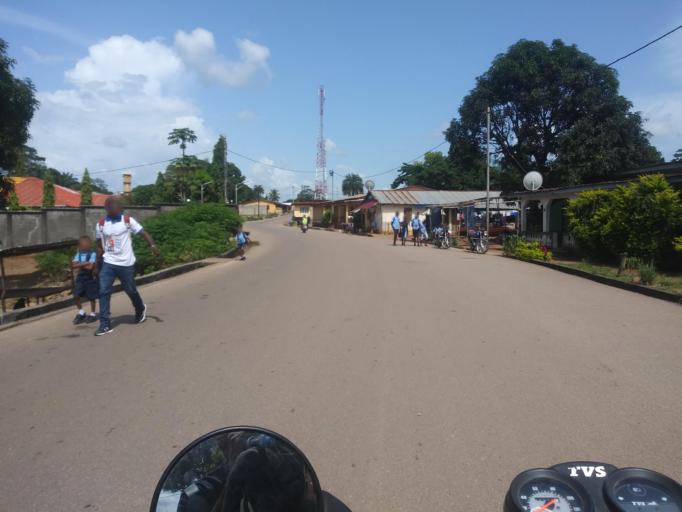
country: SL
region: Northern Province
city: Makeni
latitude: 8.8763
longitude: -12.0352
